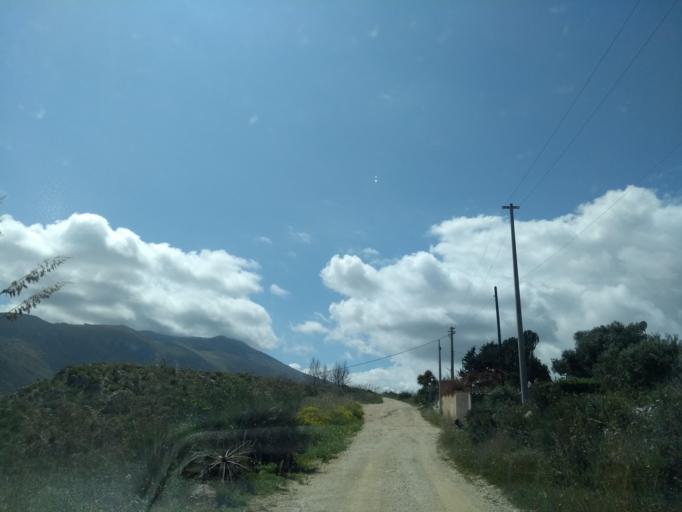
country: IT
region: Sicily
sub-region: Trapani
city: Castellammare del Golfo
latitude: 38.0504
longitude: 12.8488
